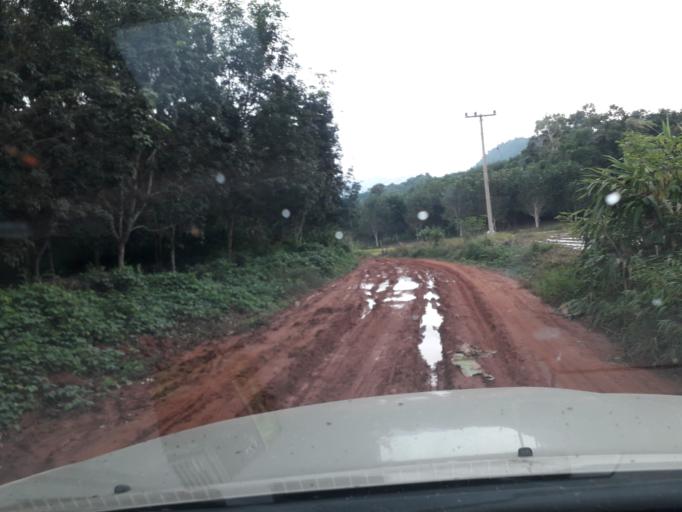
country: LA
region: Phongsali
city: Phongsali
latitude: 21.3059
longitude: 101.9722
